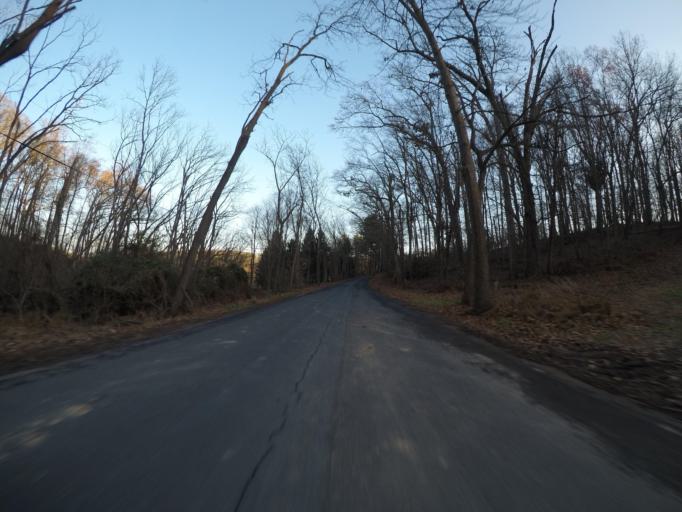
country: US
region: Maryland
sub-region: Carroll County
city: Hampstead
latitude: 39.5816
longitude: -76.8178
